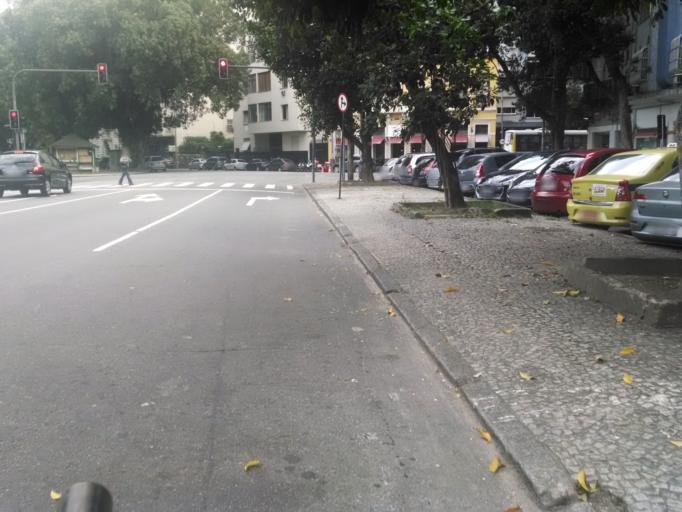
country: BR
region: Rio de Janeiro
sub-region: Rio De Janeiro
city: Rio de Janeiro
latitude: -22.9411
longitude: -43.1770
